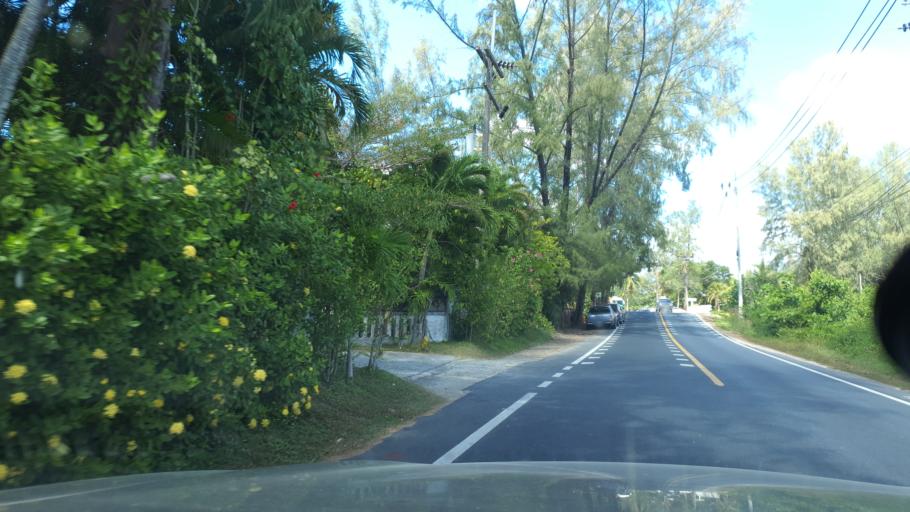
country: TH
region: Phangnga
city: Thai Mueang
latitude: 8.2859
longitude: 98.2751
